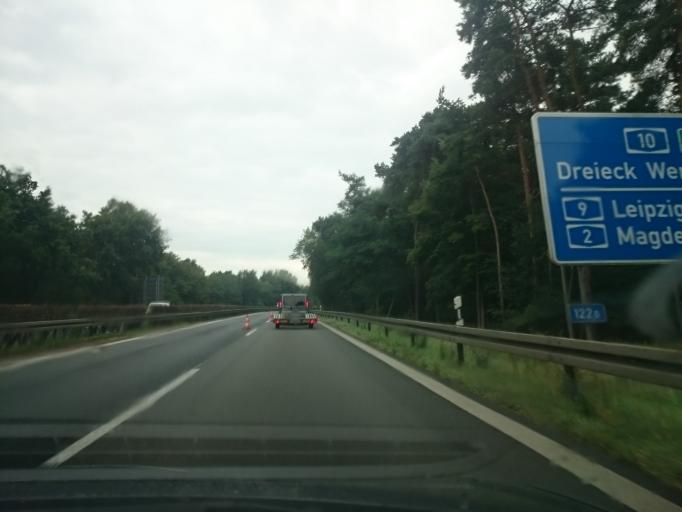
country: DE
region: Brandenburg
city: Werder
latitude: 52.4277
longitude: 12.9297
